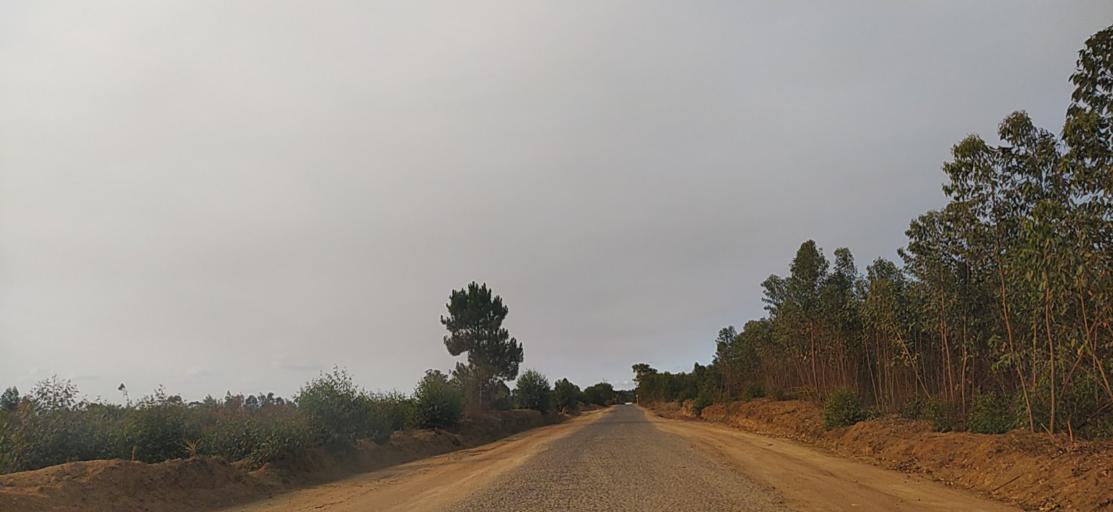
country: MG
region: Alaotra Mangoro
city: Moramanga
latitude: -18.6175
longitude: 48.2769
